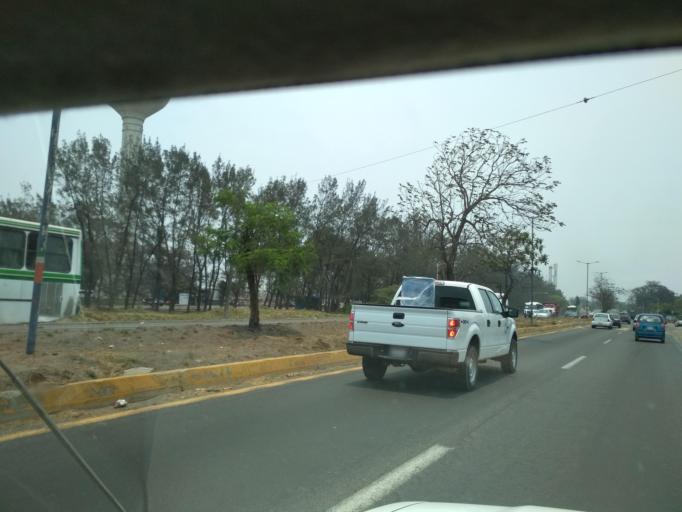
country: MX
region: Veracruz
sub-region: Veracruz
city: Oasis
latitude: 19.1762
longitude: -96.2417
